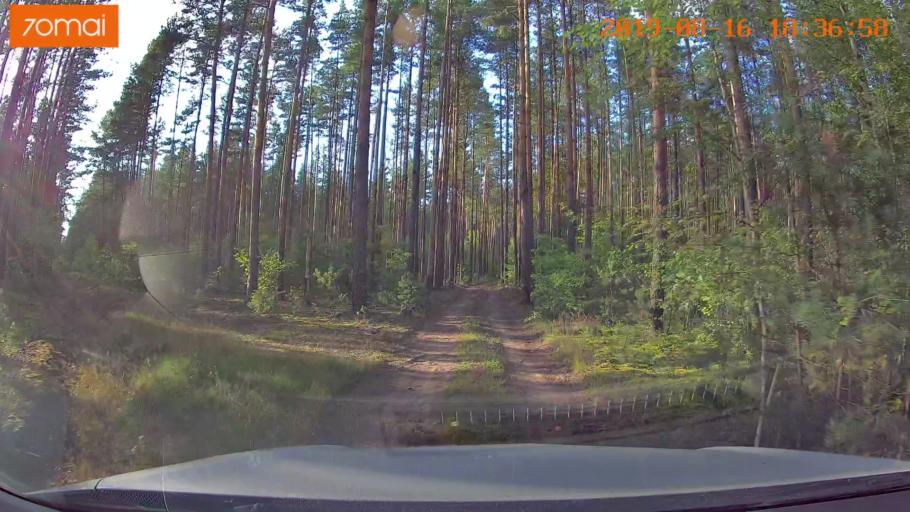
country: BY
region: Mogilev
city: Asipovichy
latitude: 53.2071
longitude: 28.6335
